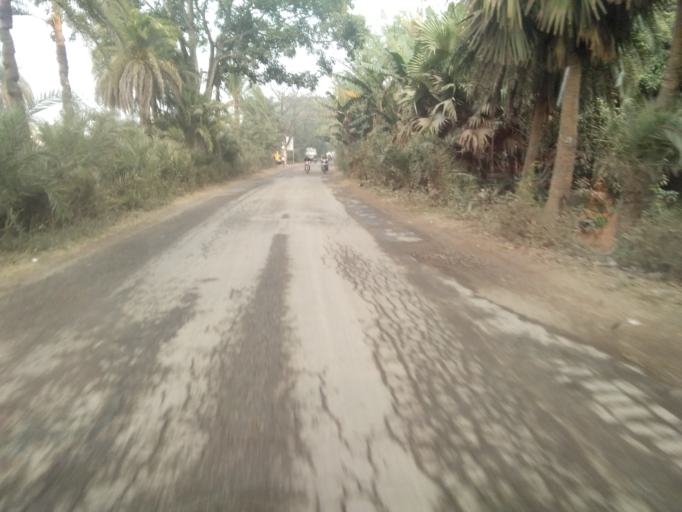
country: BD
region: Khulna
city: Satkhira
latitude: 22.6871
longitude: 89.0309
